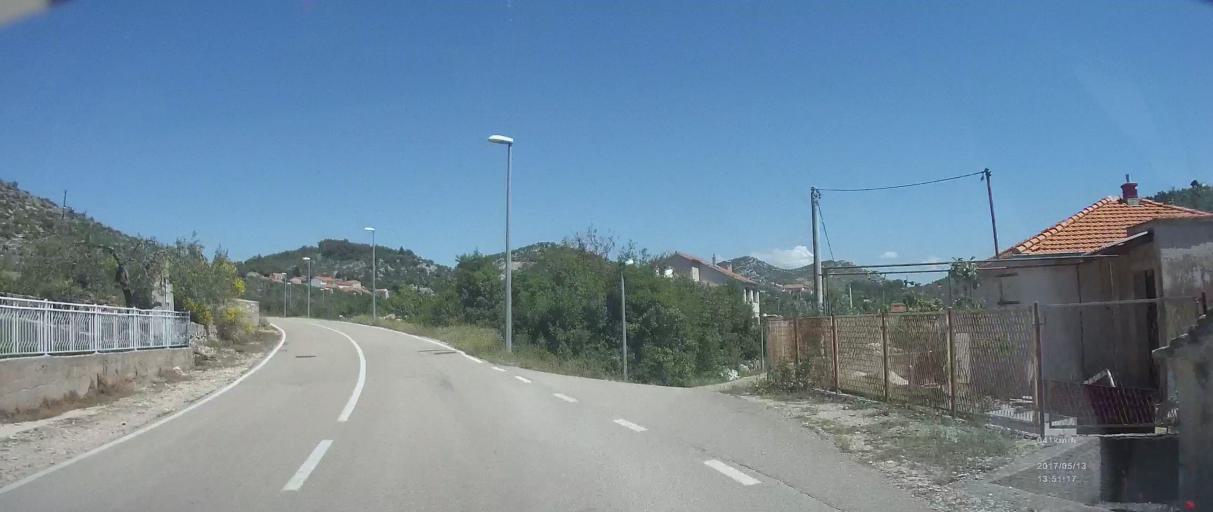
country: HR
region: Sibensko-Kniniska
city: Primosten
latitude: 43.6089
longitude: 15.9898
